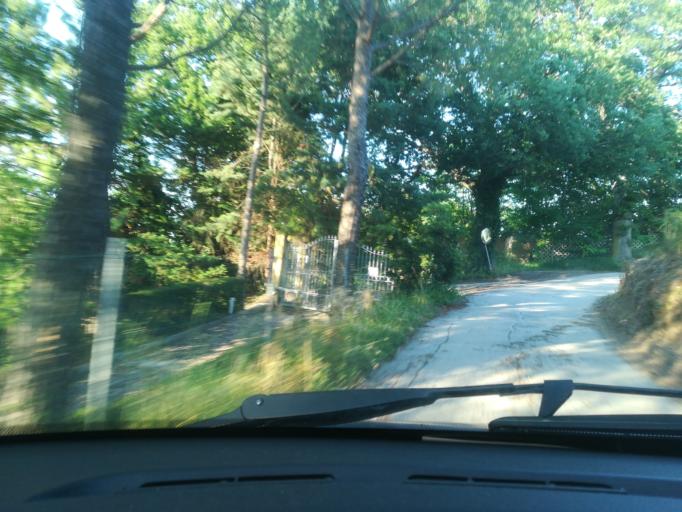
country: IT
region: The Marches
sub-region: Provincia di Macerata
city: Macerata
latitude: 43.2831
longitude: 13.4646
